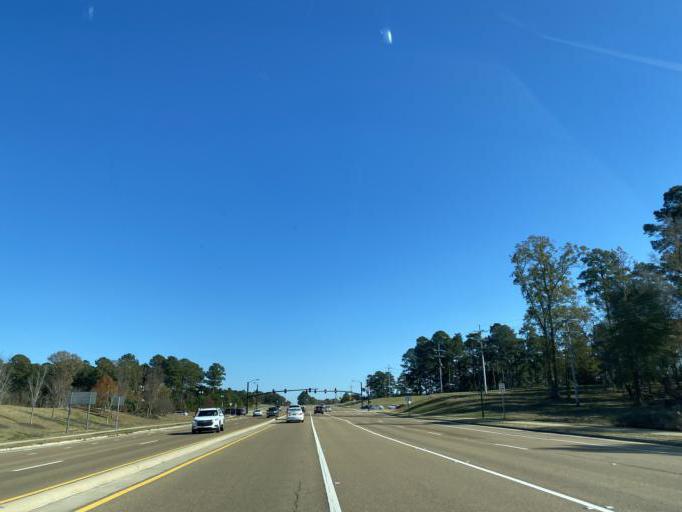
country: US
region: Mississippi
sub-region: Madison County
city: Madison
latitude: 32.4578
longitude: -90.1405
